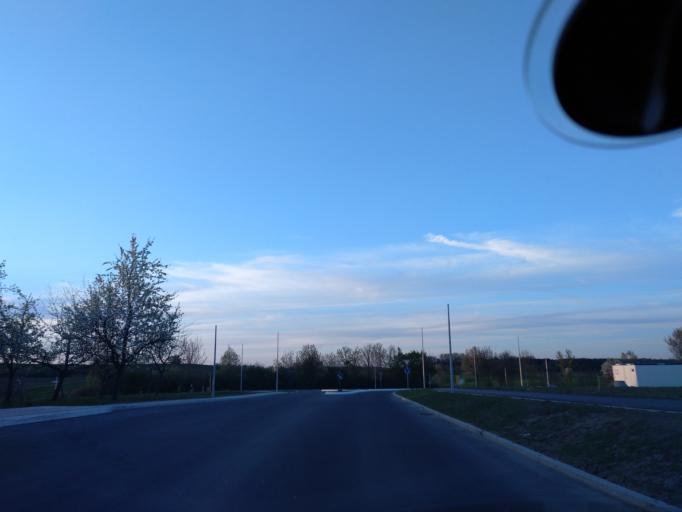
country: DE
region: Baden-Wuerttemberg
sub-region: Regierungsbezirk Stuttgart
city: Satteldorf
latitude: 49.1715
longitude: 10.0876
